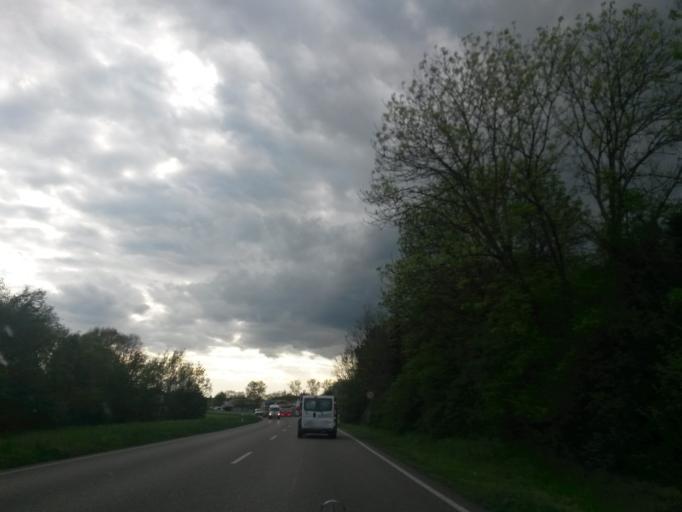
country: DE
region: Baden-Wuerttemberg
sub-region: Regierungsbezirk Stuttgart
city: Mogglingen
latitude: 48.8228
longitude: 9.9752
